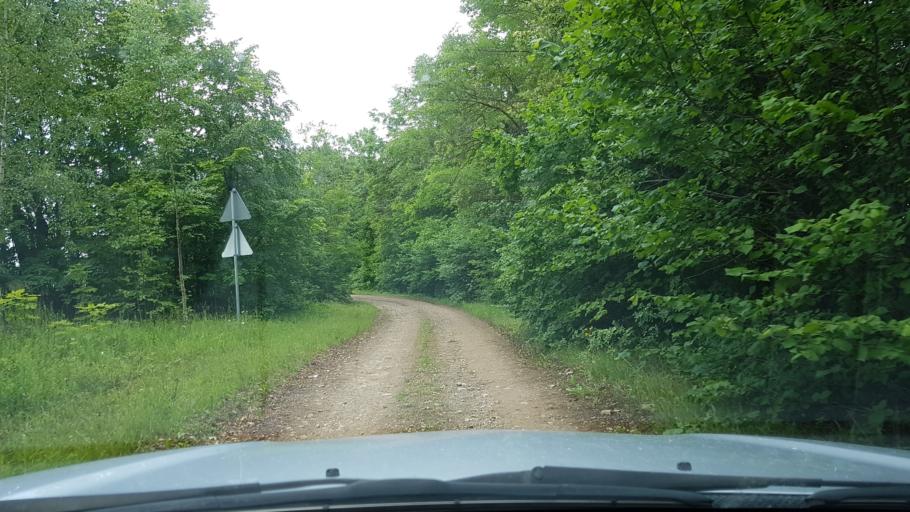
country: EE
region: Ida-Virumaa
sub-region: Narva-Joesuu linn
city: Narva-Joesuu
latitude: 59.4016
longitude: 27.9739
